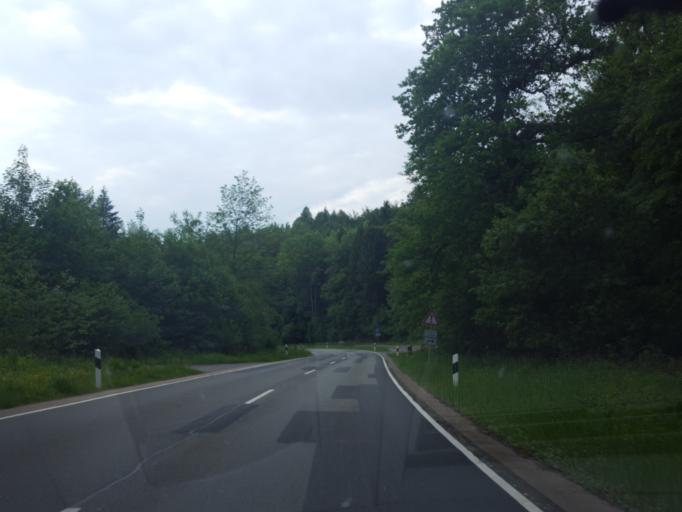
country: DE
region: Lower Saxony
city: Bad Grund
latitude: 51.8274
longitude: 10.2132
